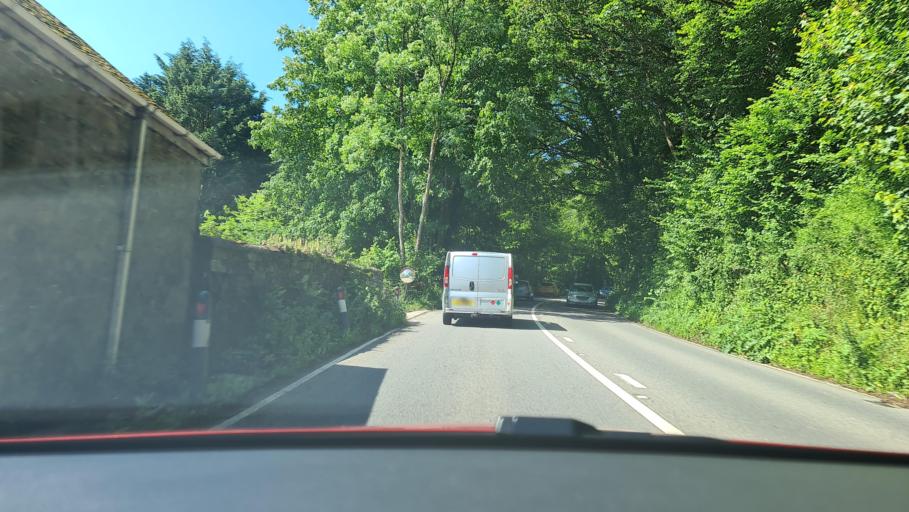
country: GB
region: England
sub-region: Cornwall
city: Lostwithiel
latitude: 50.4046
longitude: -4.6759
